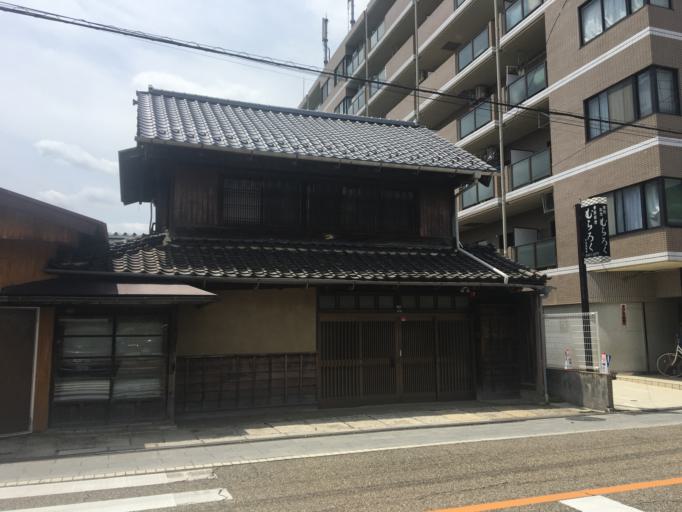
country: JP
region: Saitama
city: Shimotoda
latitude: 35.8264
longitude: 139.6775
